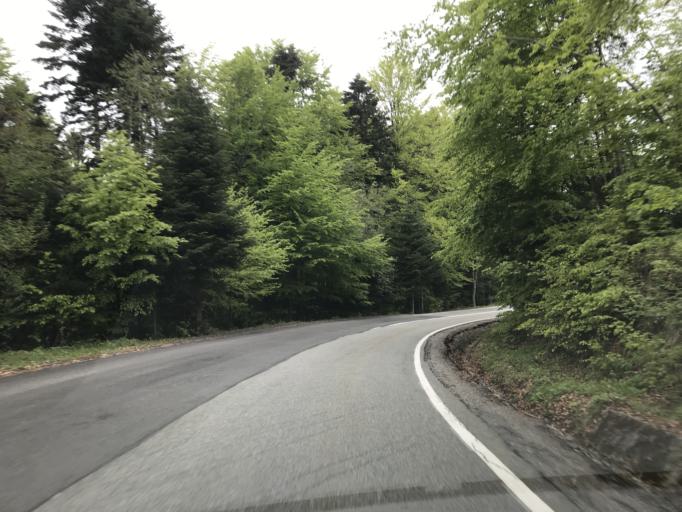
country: RO
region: Sibiu
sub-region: Comuna Cartisoara
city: Cartisoara
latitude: 45.6637
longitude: 24.5912
